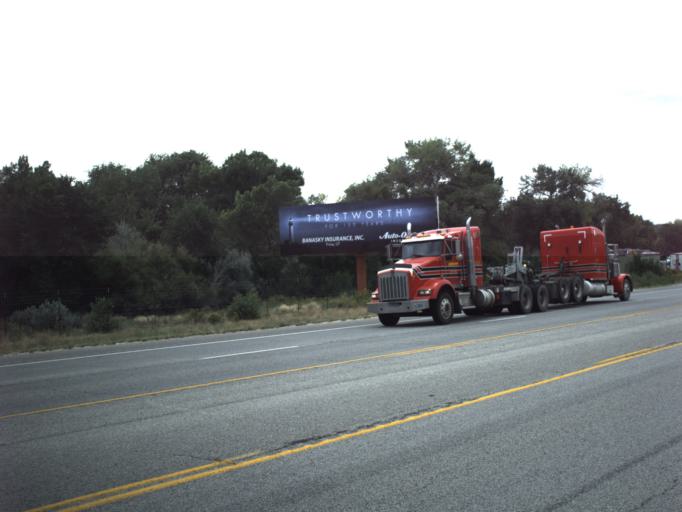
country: US
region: Utah
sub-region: Carbon County
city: Spring Glen
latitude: 39.6652
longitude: -110.8612
